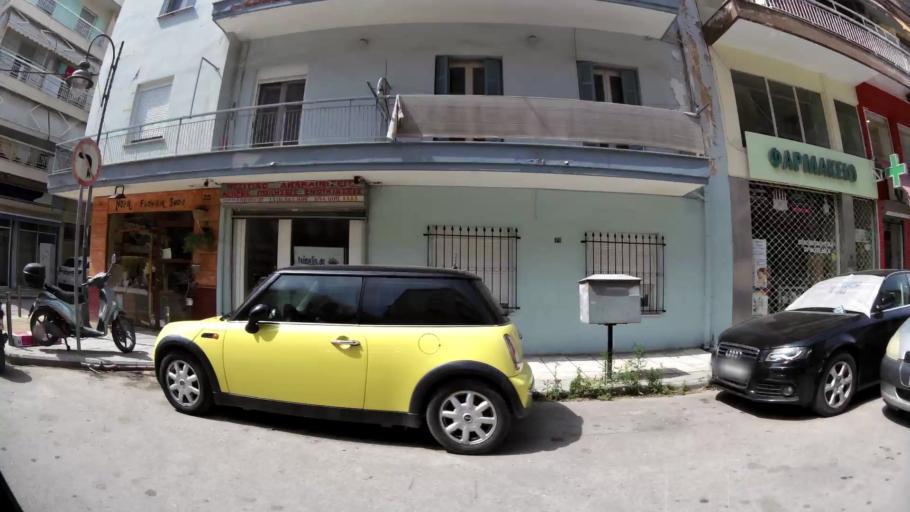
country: GR
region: Central Macedonia
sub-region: Nomos Thessalonikis
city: Kalamaria
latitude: 40.6043
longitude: 22.9556
